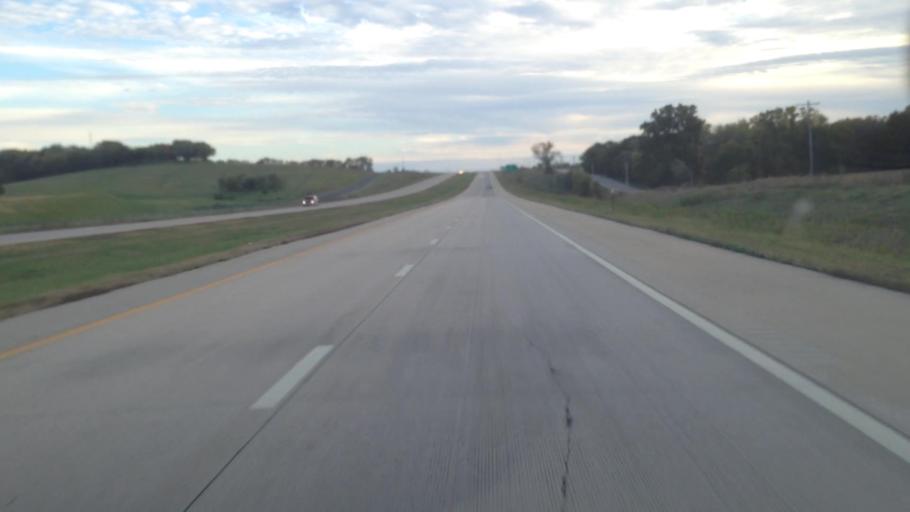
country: US
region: Kansas
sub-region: Douglas County
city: Baldwin City
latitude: 38.8006
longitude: -95.2692
